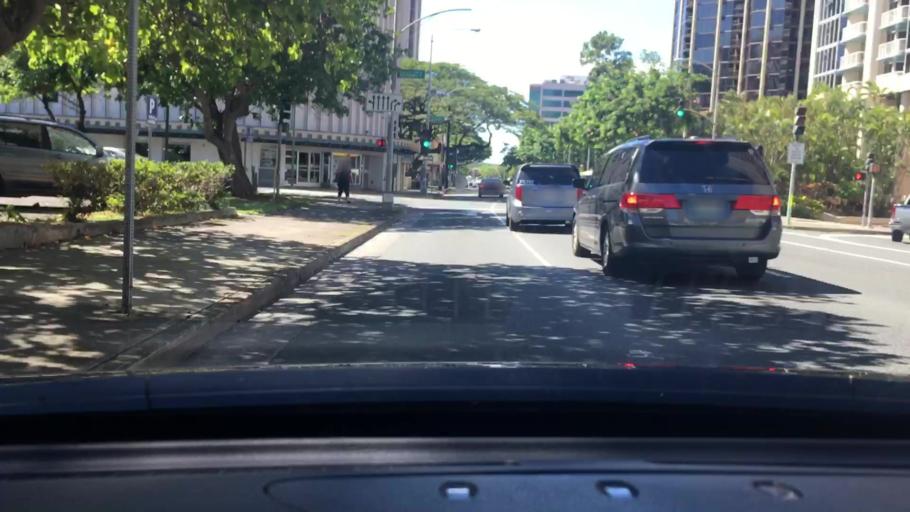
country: US
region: Hawaii
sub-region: Honolulu County
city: Honolulu
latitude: 21.3119
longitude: -157.8599
